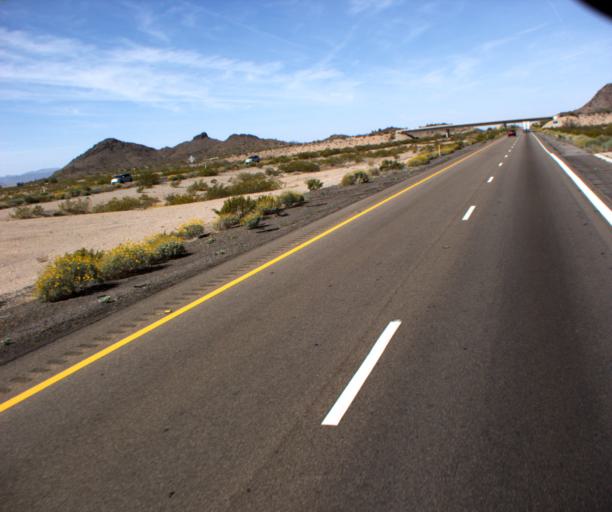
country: US
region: Arizona
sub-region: La Paz County
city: Salome
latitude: 33.6088
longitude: -113.6158
